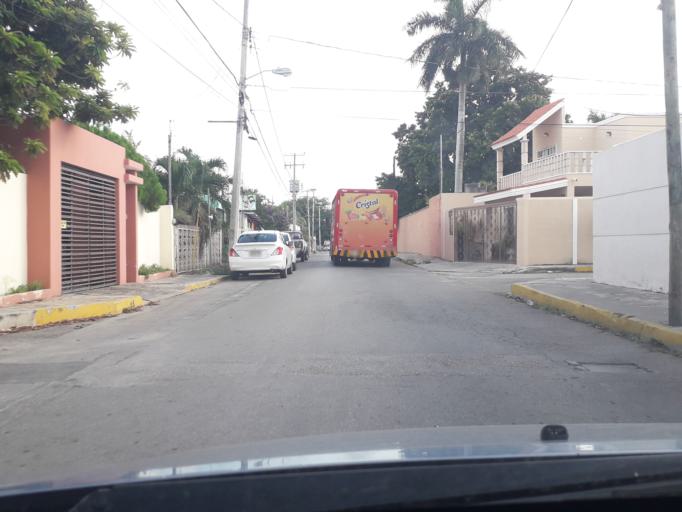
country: MX
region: Yucatan
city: Merida
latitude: 21.0103
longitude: -89.6364
